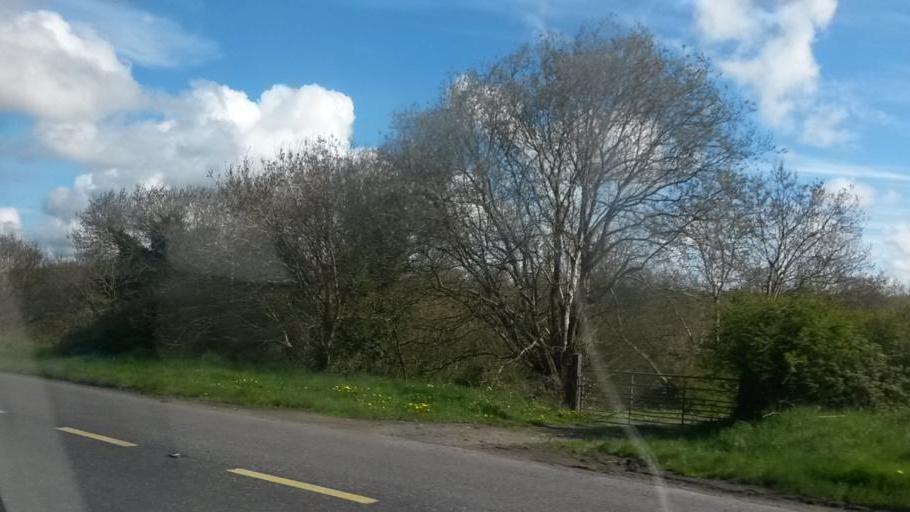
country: IE
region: Ulster
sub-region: An Cabhan
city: Virginia
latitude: 53.7869
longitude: -7.0199
